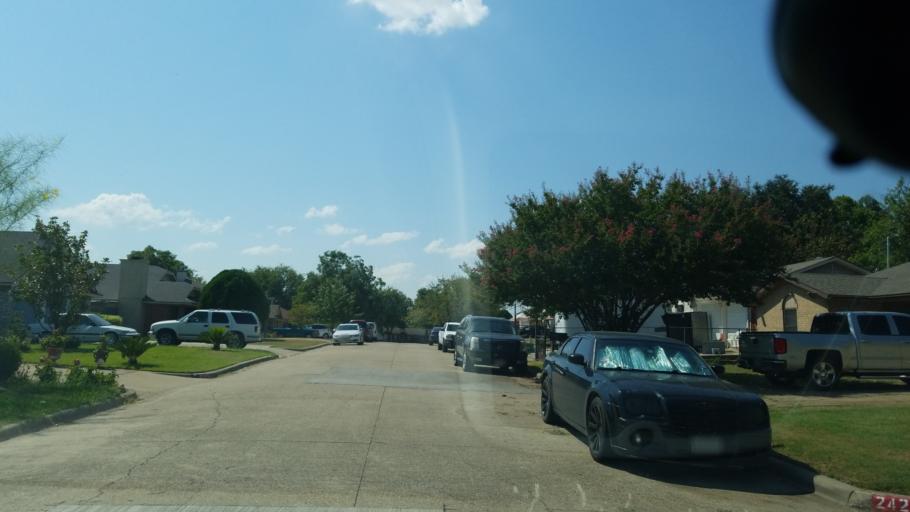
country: US
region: Texas
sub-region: Dallas County
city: Grand Prairie
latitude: 32.7094
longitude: -96.9798
